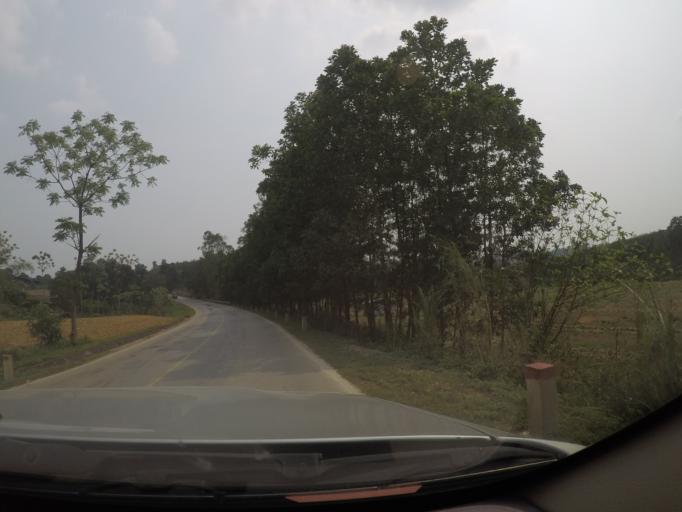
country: VN
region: Thanh Hoa
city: Thi Tran Yen Cat
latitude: 19.4944
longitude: 105.3922
